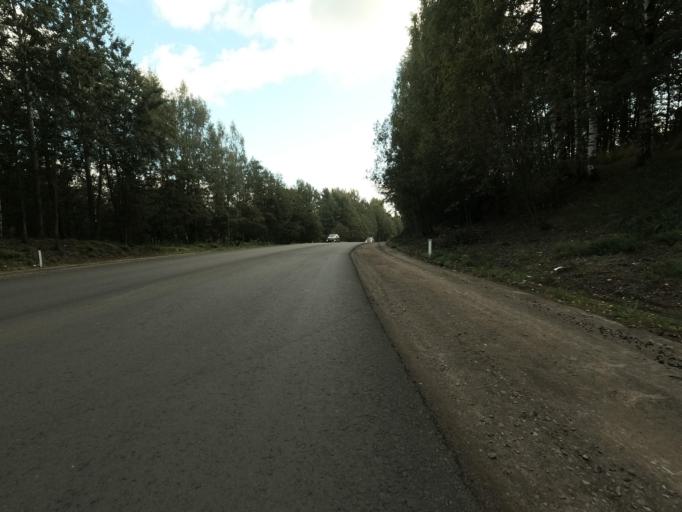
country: RU
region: Leningrad
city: Koltushi
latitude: 59.9664
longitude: 30.6582
